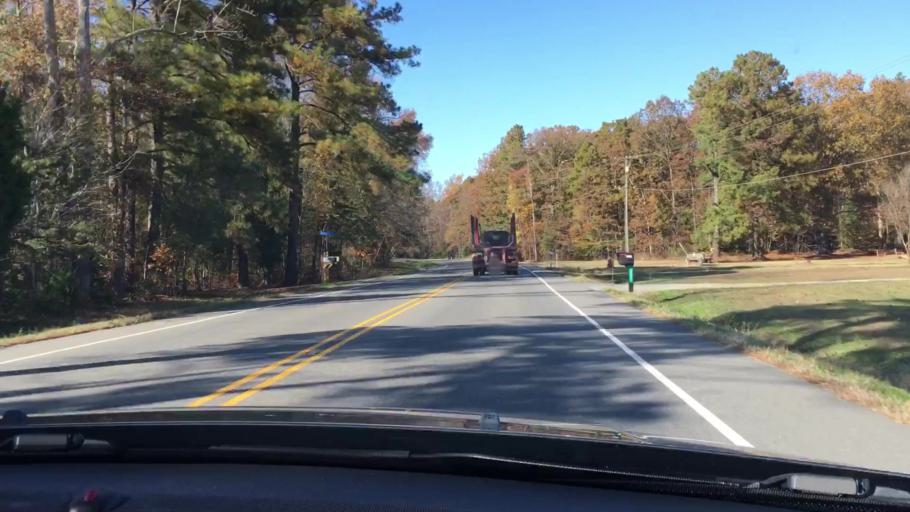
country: US
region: Virginia
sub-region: King William County
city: Central Garage
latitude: 37.7713
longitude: -77.1554
